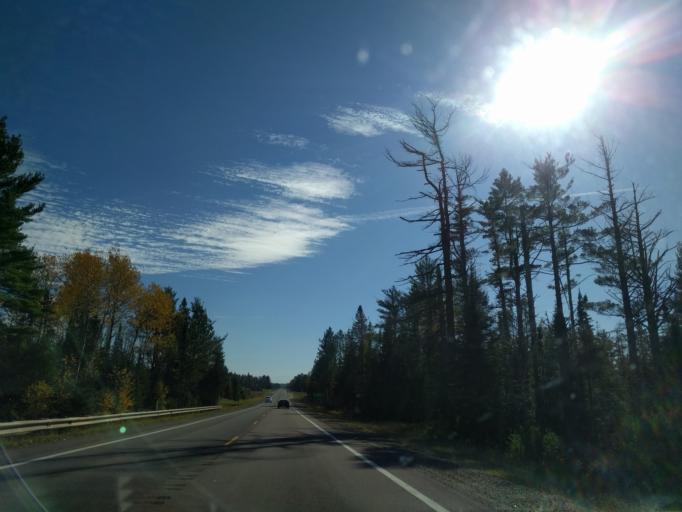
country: US
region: Michigan
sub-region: Marquette County
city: West Ishpeming
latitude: 46.3940
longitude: -87.9974
